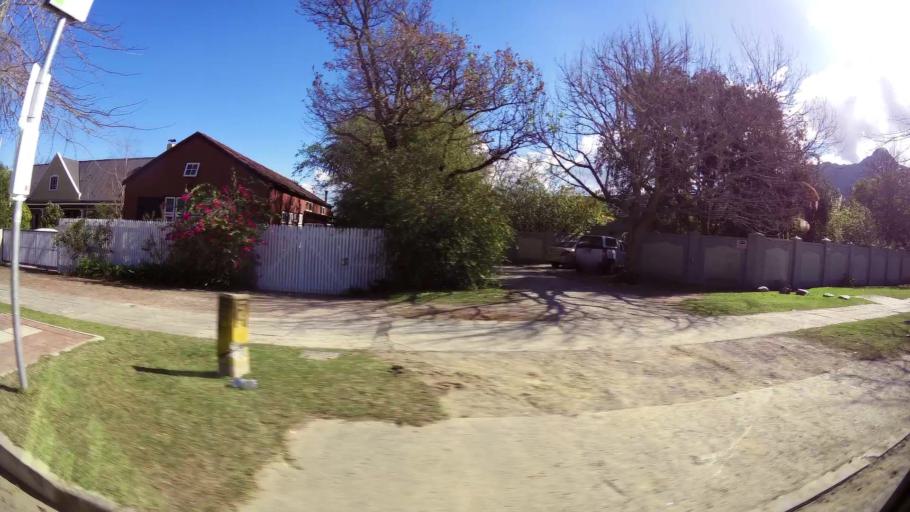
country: ZA
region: Western Cape
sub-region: Eden District Municipality
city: George
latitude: -33.9531
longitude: 22.4600
